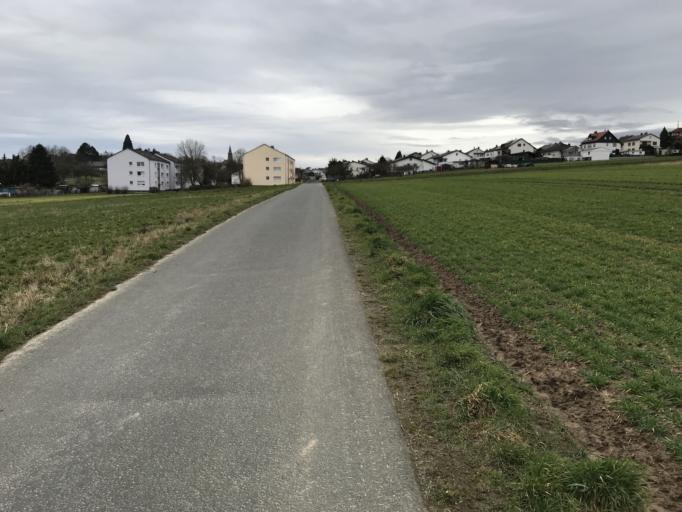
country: DE
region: Hesse
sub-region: Regierungsbezirk Giessen
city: Heuchelheim
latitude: 50.5917
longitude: 8.6200
